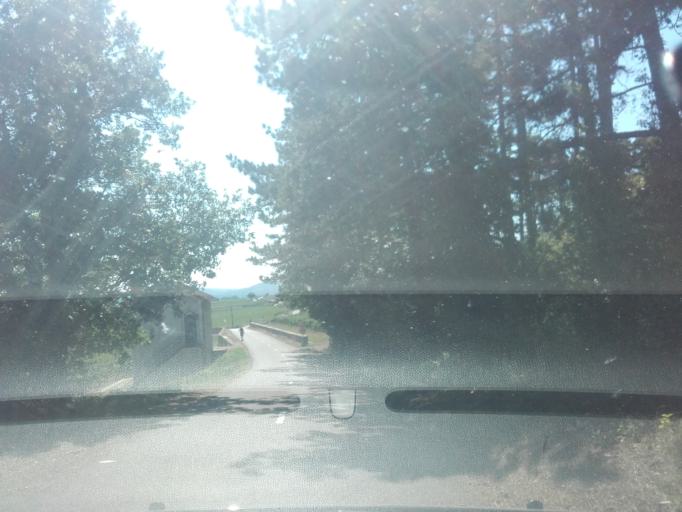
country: FR
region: Bourgogne
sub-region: Departement de la Cote-d'Or
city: Corpeau
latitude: 46.9543
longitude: 4.7464
